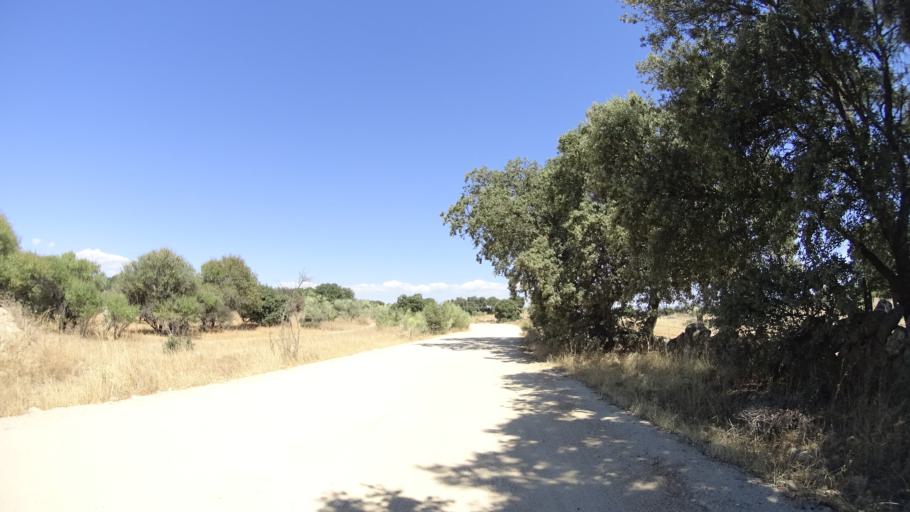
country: ES
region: Madrid
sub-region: Provincia de Madrid
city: Colmenarejo
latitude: 40.5324
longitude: -4.0107
